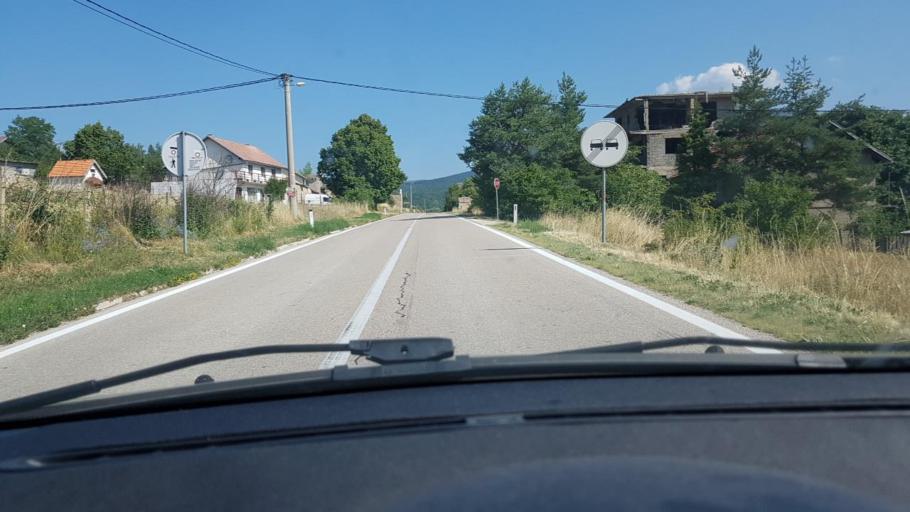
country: BA
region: Federation of Bosnia and Herzegovina
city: Bosansko Grahovo
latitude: 44.0790
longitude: 16.5710
